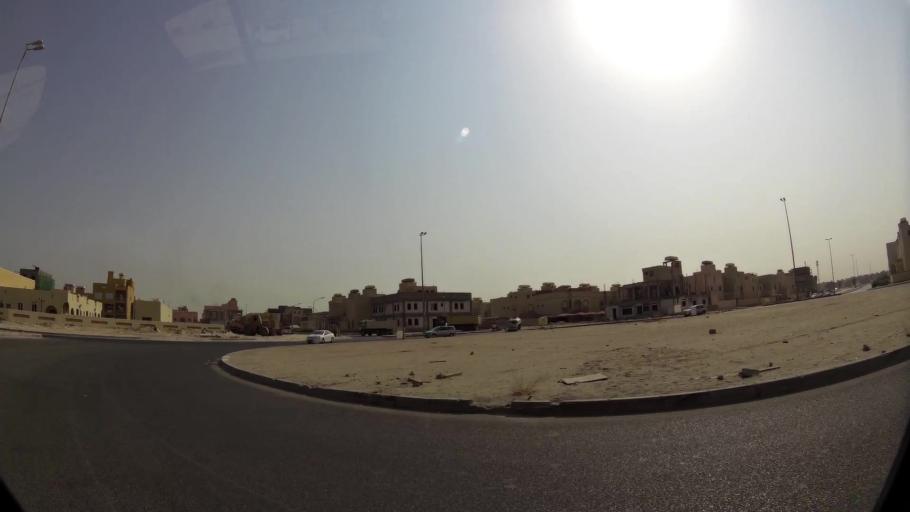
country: KW
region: Muhafazat al Jahra'
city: Al Jahra'
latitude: 29.3490
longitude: 47.7587
